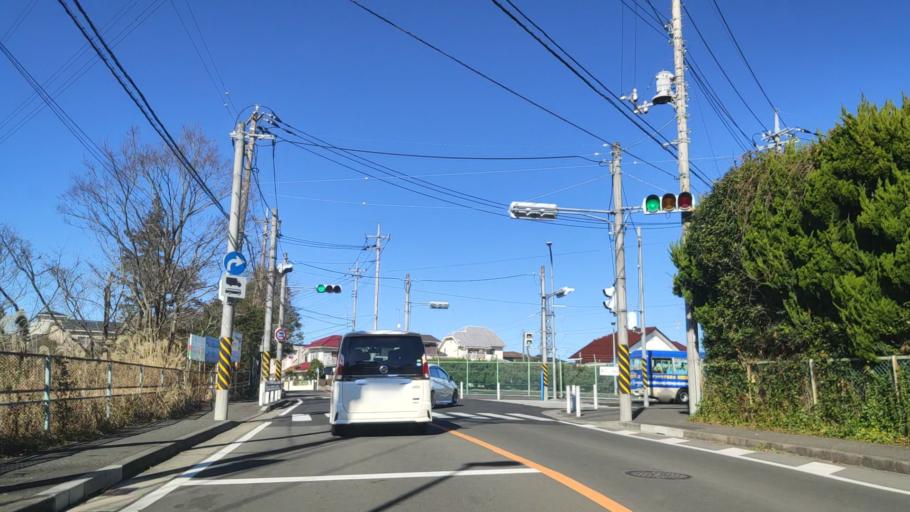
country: JP
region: Kanagawa
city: Minami-rinkan
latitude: 35.5086
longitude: 139.4991
